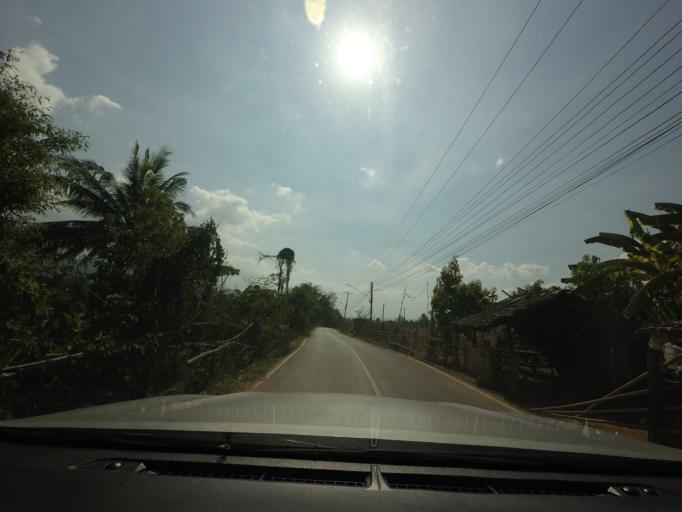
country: TH
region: Mae Hong Son
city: Wiang Nuea
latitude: 19.3918
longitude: 98.4428
